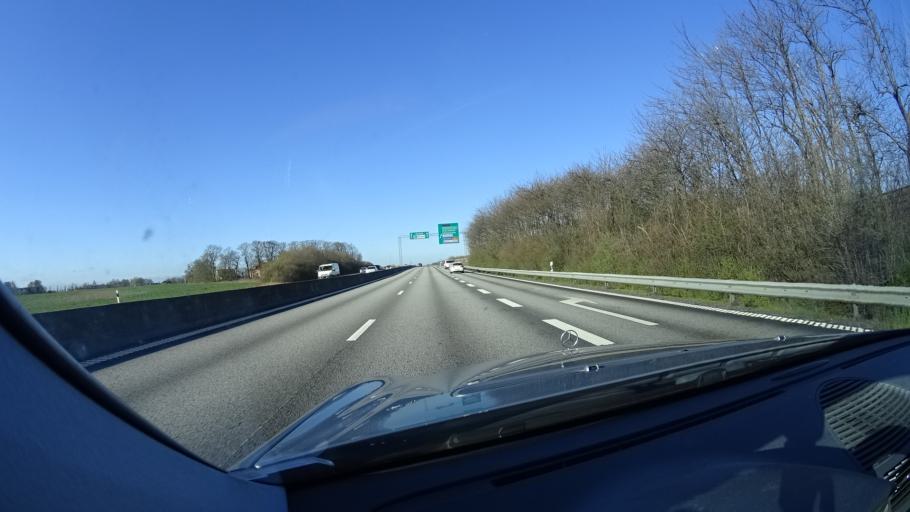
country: SE
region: Skane
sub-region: Staffanstorps Kommun
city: Hjaerup
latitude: 55.6460
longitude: 13.1148
